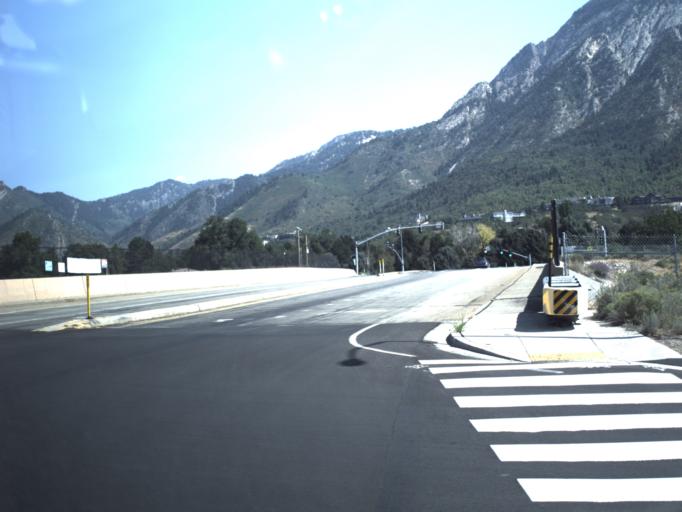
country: US
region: Utah
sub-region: Salt Lake County
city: Mount Olympus
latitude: 40.6746
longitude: -111.8033
